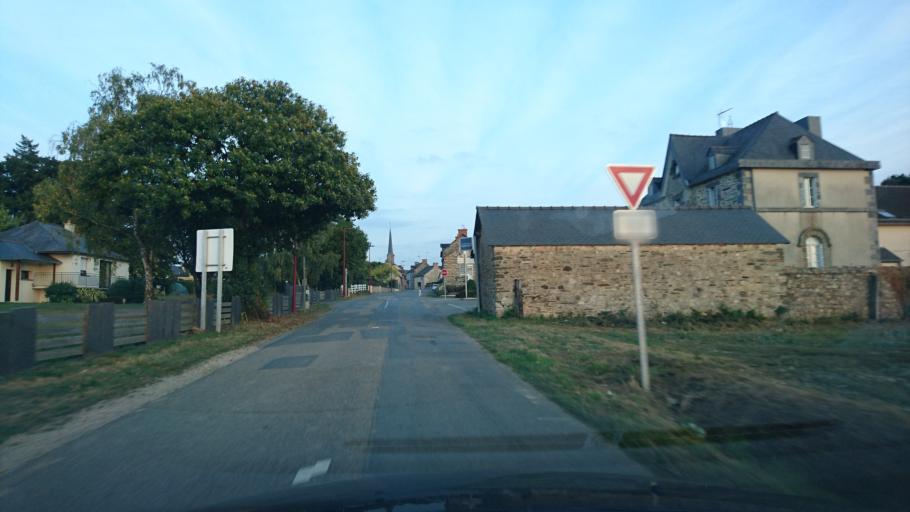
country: FR
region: Brittany
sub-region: Departement d'Ille-et-Vilaine
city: Maure-de-Bretagne
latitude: 47.8888
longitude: -2.0464
